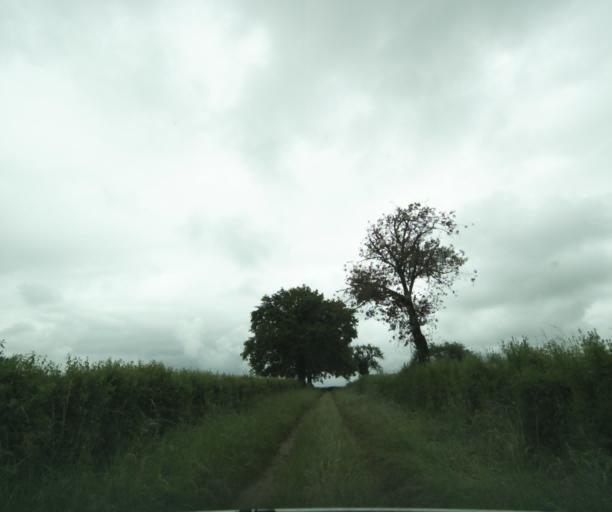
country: FR
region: Bourgogne
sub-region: Departement de Saone-et-Loire
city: Charolles
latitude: 46.4592
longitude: 4.3548
